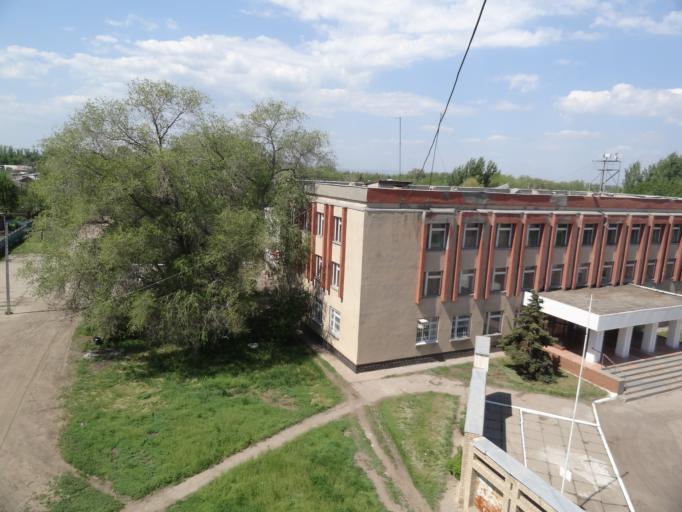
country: RU
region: Saratov
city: Privolzhskiy
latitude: 51.3899
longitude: 46.1262
